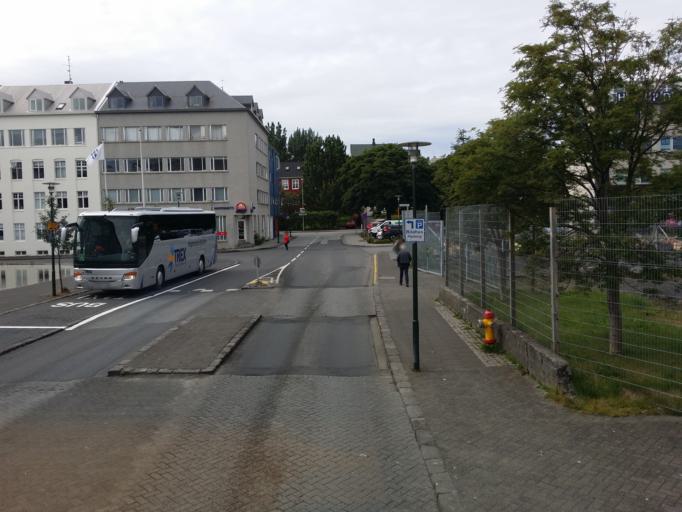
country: IS
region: Capital Region
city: Kopavogur
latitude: 64.1464
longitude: -21.9419
